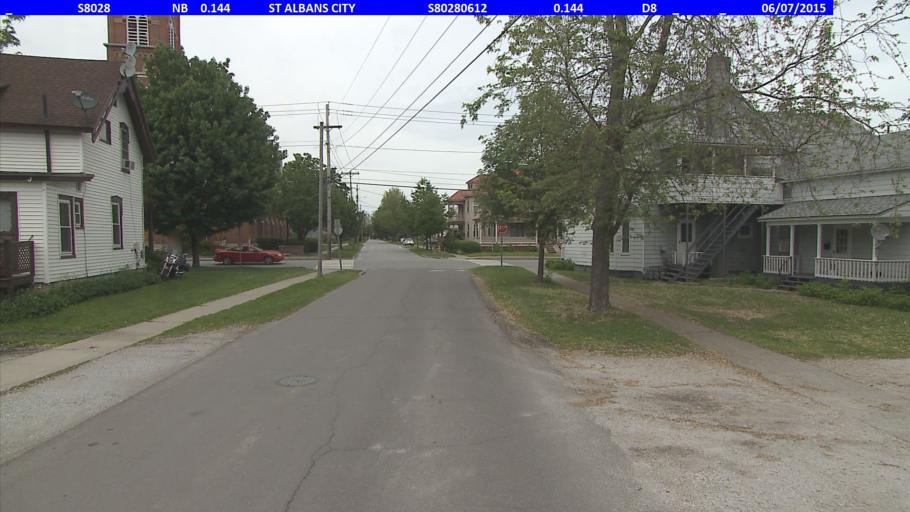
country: US
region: Vermont
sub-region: Franklin County
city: Saint Albans
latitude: 44.8108
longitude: -73.0927
